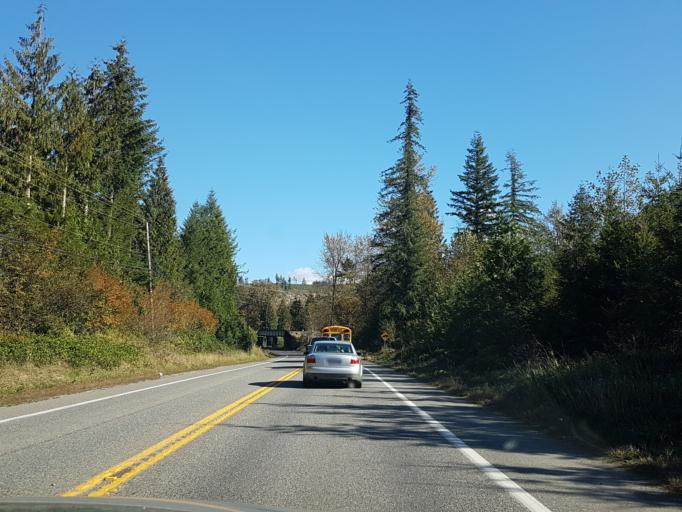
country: US
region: Washington
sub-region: Snohomish County
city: Gold Bar
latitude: 47.8351
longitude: -121.6505
